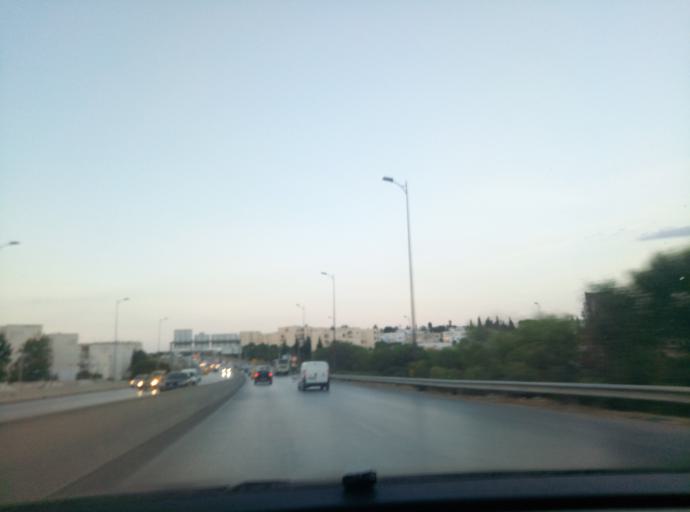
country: TN
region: Tunis
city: Tunis
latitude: 36.8221
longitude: 10.1394
